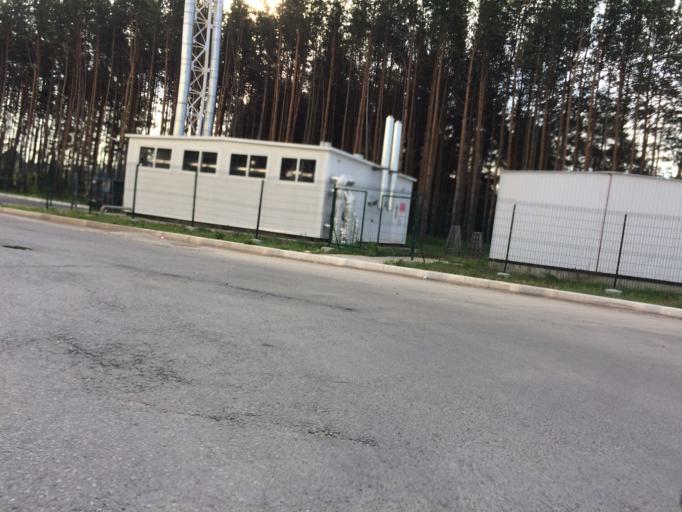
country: RU
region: Mariy-El
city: Yoshkar-Ola
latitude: 56.6268
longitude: 47.9302
